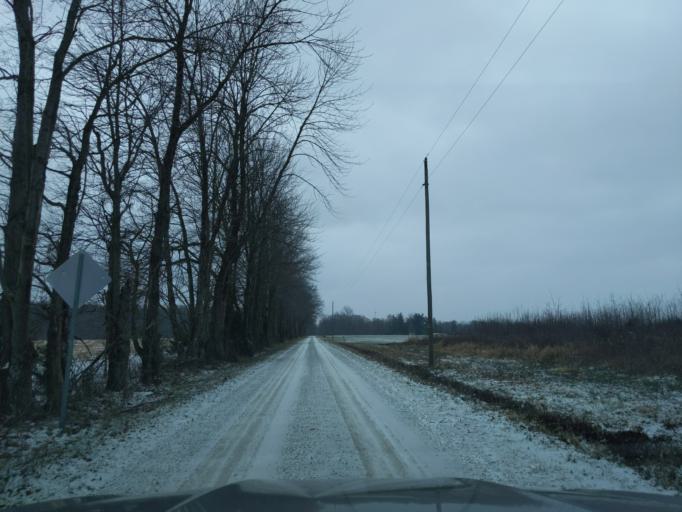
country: US
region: Indiana
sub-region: Decatur County
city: Westport
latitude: 39.2045
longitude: -85.4585
